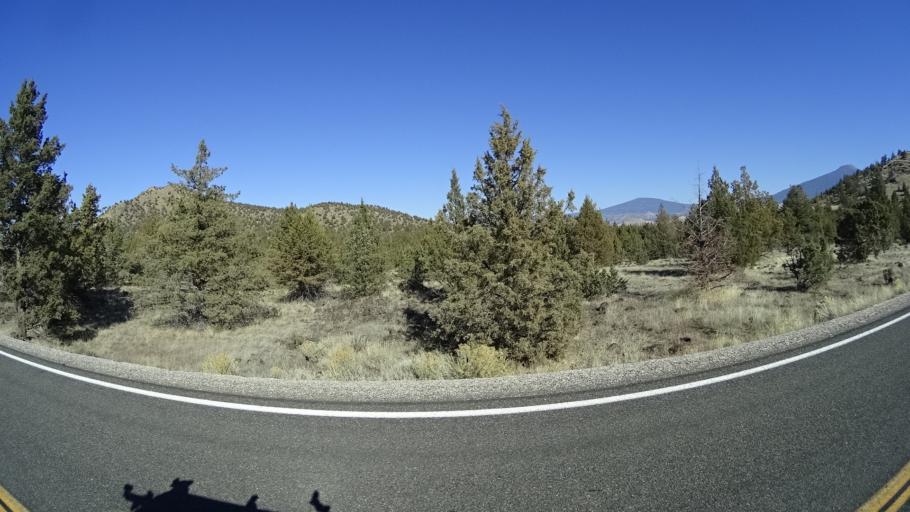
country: US
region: California
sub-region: Siskiyou County
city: Montague
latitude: 41.6595
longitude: -122.3782
